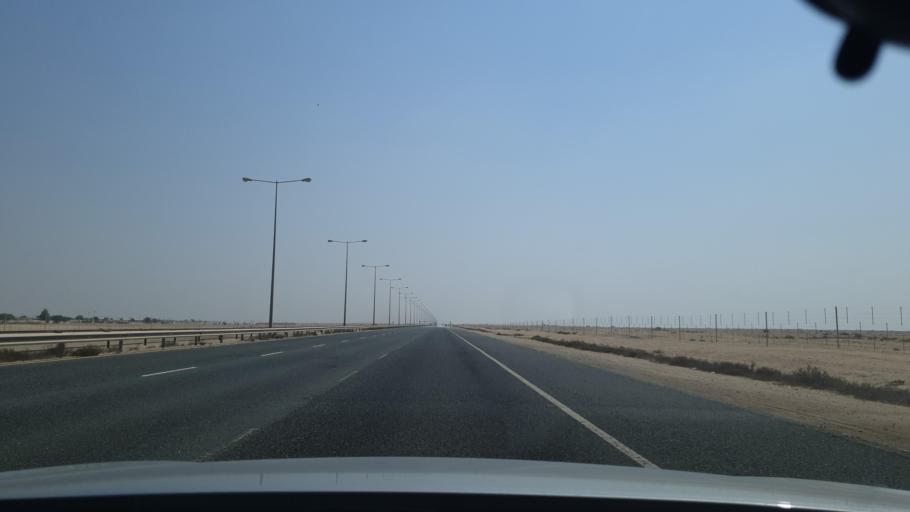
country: QA
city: Al Ghuwayriyah
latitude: 25.8139
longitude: 51.3714
